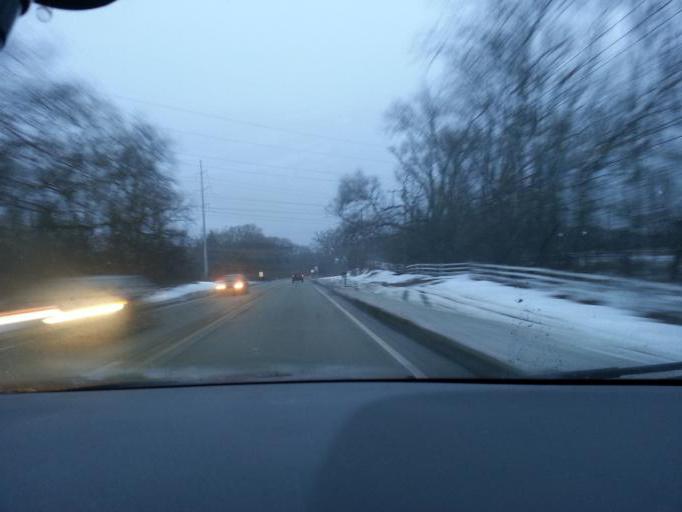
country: US
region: Illinois
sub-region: Kane County
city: Carpentersville
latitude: 42.1361
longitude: -88.2374
